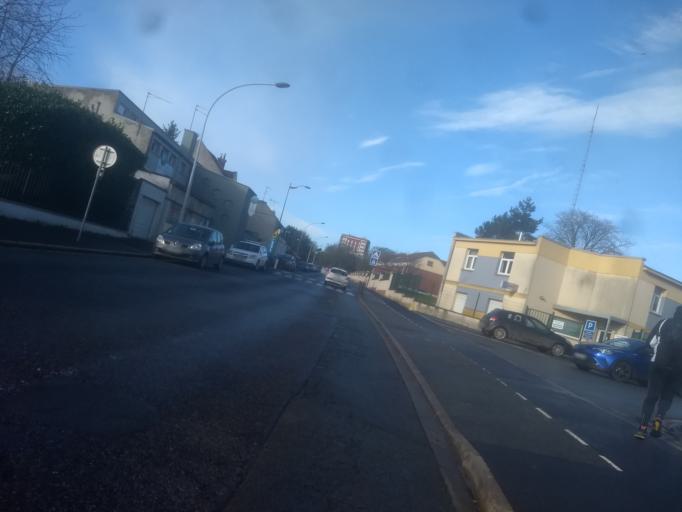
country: FR
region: Nord-Pas-de-Calais
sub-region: Departement du Pas-de-Calais
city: Achicourt
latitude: 50.2922
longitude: 2.7535
